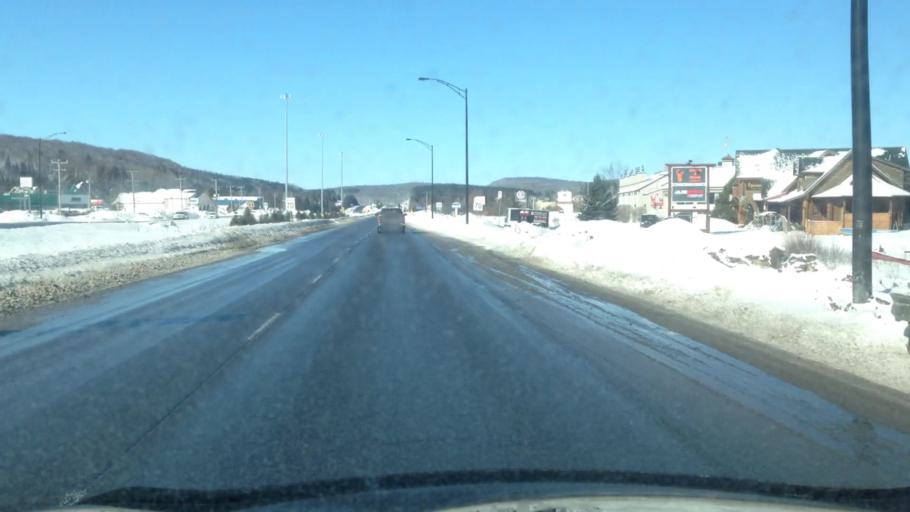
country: CA
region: Quebec
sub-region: Laurentides
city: Mont-Tremblant
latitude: 46.1169
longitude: -74.5652
